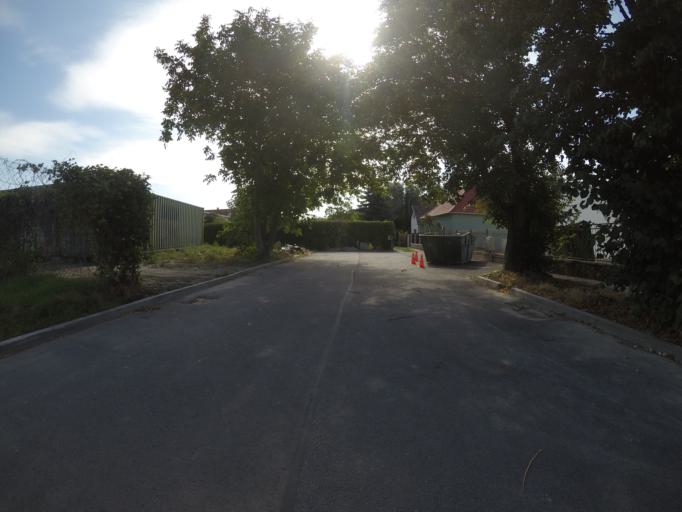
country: SK
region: Trnavsky
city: Dunajska Streda
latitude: 47.9880
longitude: 17.6259
